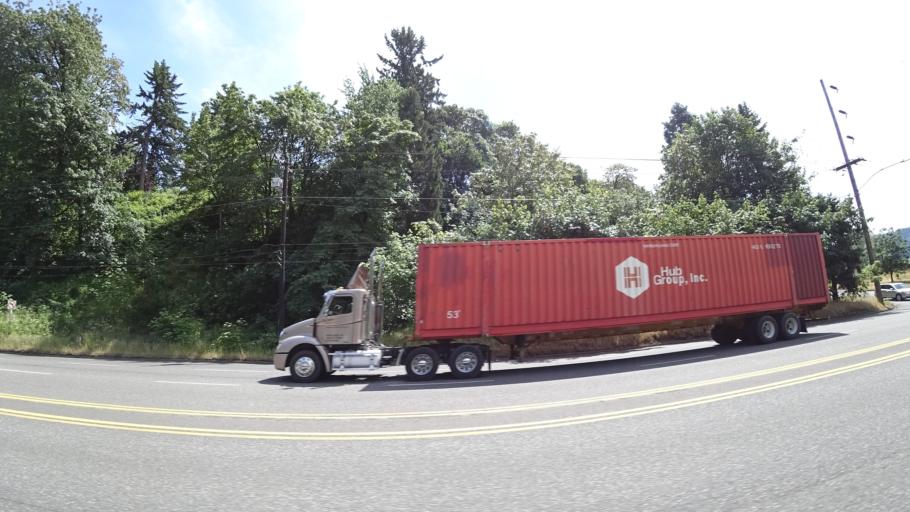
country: US
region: Oregon
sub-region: Multnomah County
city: Portland
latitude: 45.5560
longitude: -122.6905
